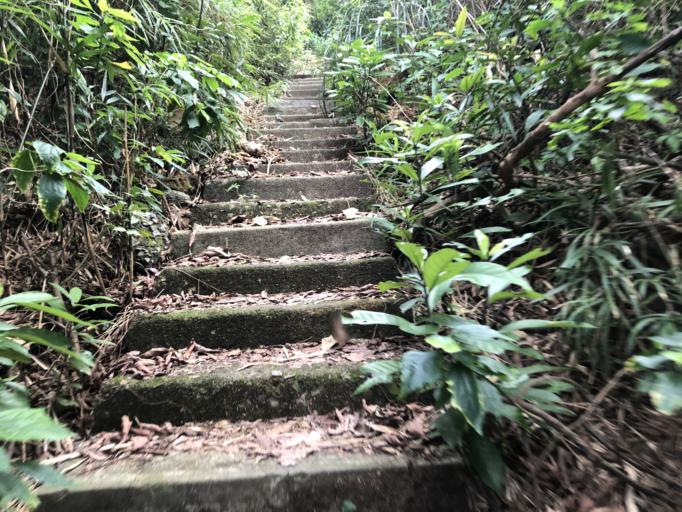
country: HK
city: Hong Kong
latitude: 22.2792
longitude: 114.1196
